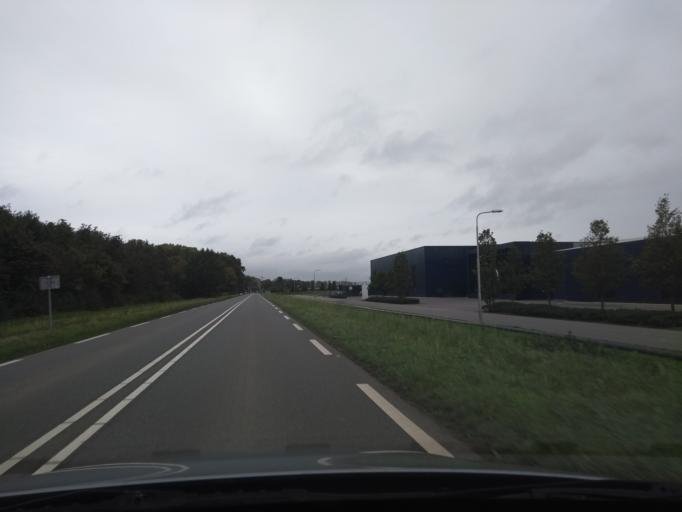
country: NL
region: Overijssel
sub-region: Gemeente Steenwijkerland
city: Blokzijl
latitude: 52.7374
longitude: 5.8587
